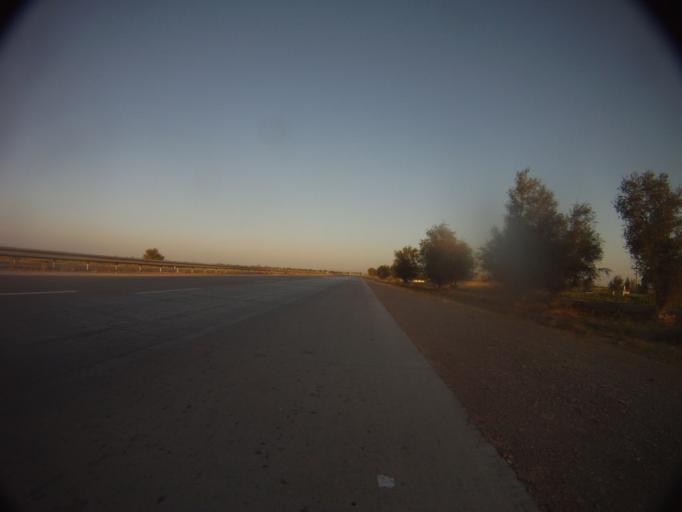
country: KZ
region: Ongtustik Qazaqstan
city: Turkestan
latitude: 43.2687
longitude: 68.3542
